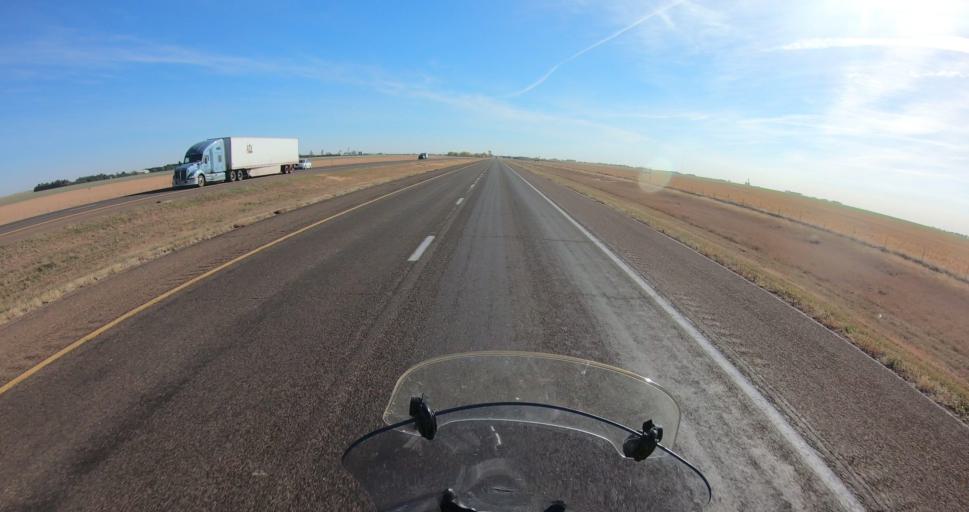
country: US
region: Kansas
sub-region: Sherman County
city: Goodland
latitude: 39.3289
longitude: -101.7614
